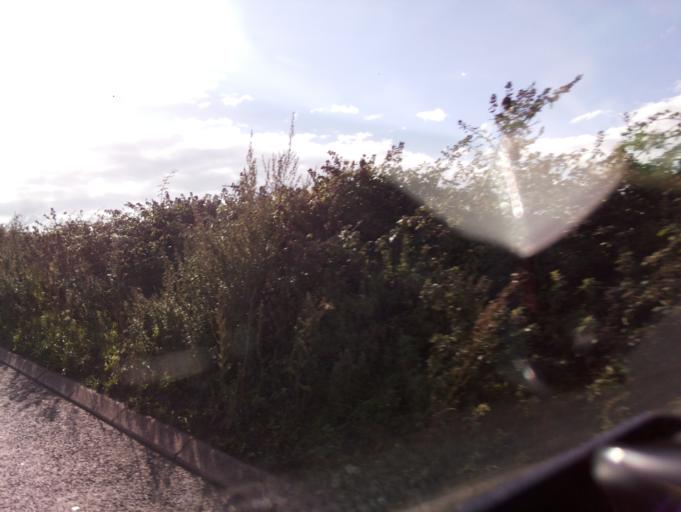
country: GB
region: England
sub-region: Devon
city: Exminster
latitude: 50.6898
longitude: -3.5266
